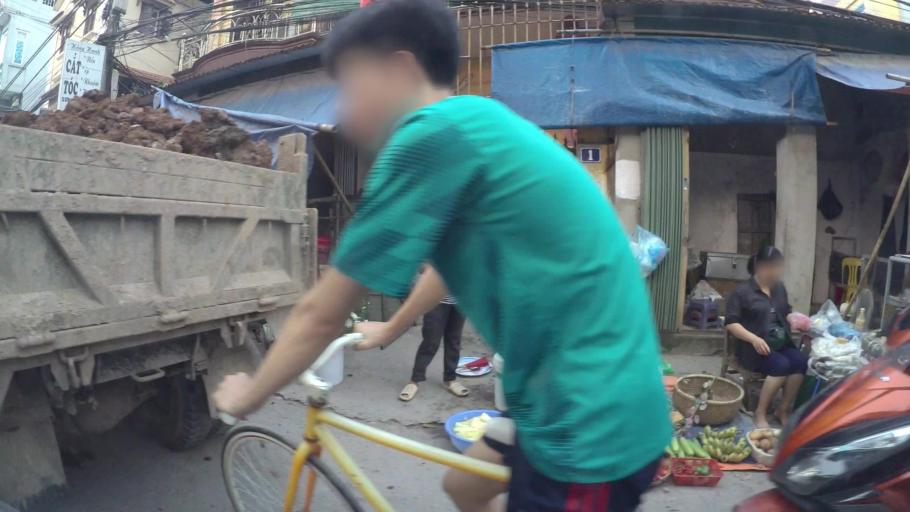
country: VN
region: Ha Noi
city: Ha Dong
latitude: 20.9933
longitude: 105.7297
